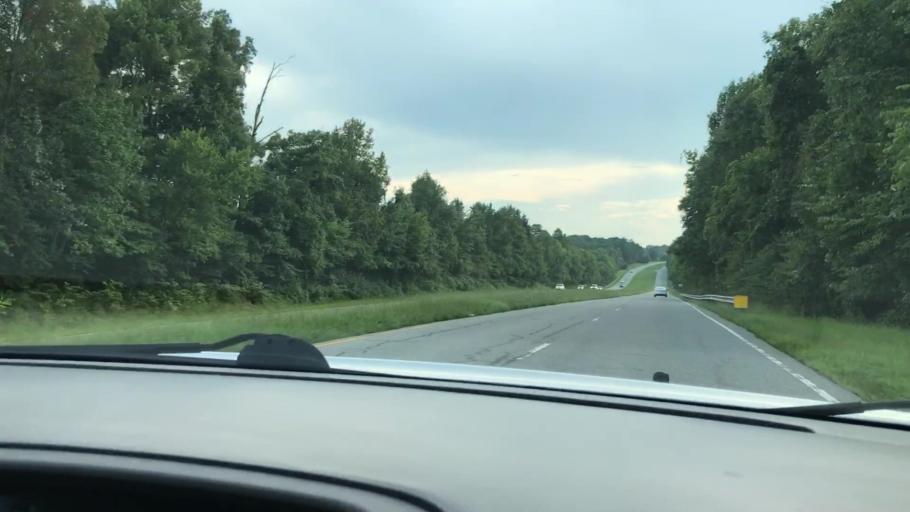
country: US
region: North Carolina
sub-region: Davidson County
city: Denton
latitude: 35.6056
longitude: -80.0255
